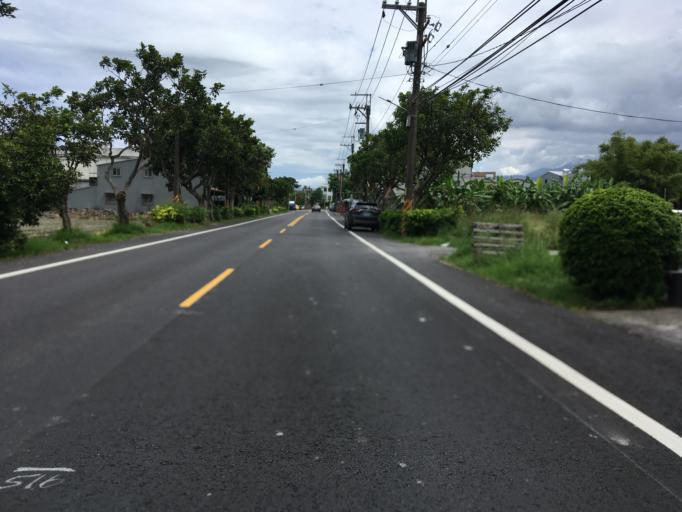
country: TW
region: Taiwan
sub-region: Yilan
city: Yilan
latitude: 24.6893
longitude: 121.7971
